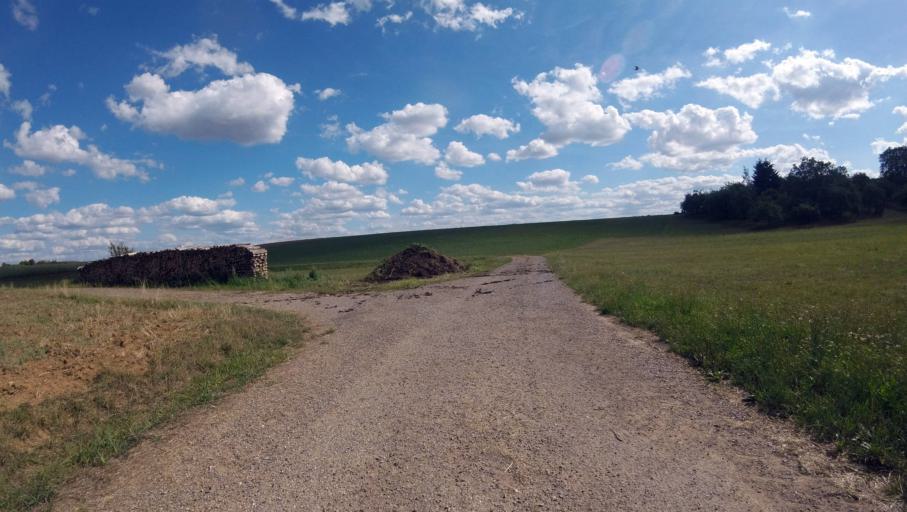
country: DE
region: Baden-Wuerttemberg
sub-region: Regierungsbezirk Stuttgart
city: Aspach
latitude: 48.9936
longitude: 9.3733
